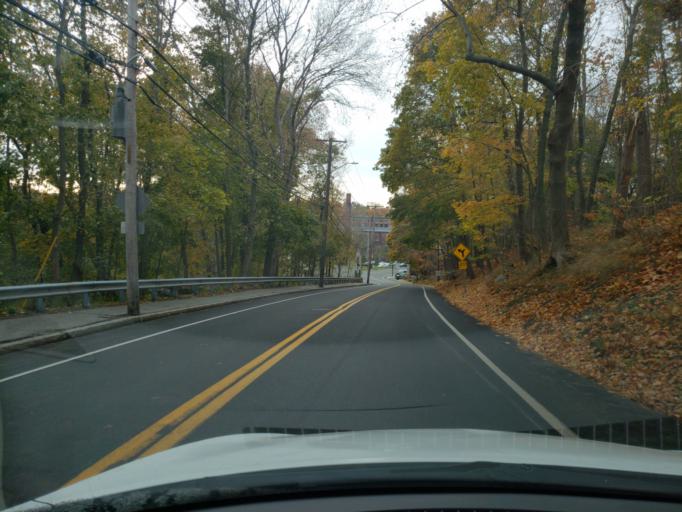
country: US
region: Massachusetts
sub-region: Essex County
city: Andover
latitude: 42.6585
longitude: -71.1480
